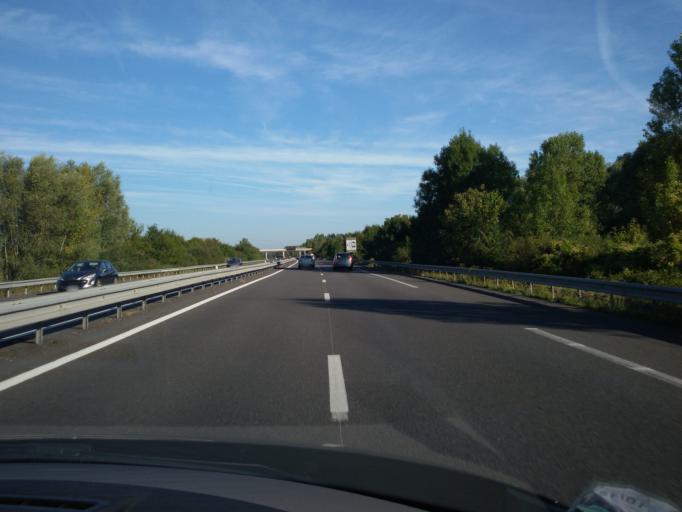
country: FR
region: Centre
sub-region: Departement du Cher
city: Foecy
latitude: 47.1831
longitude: 2.1720
